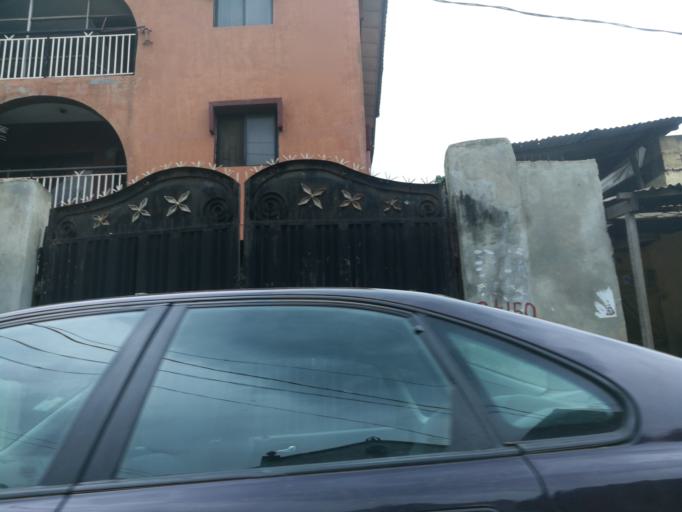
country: NG
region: Lagos
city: Ebute Metta
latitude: 6.4857
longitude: 3.3831
